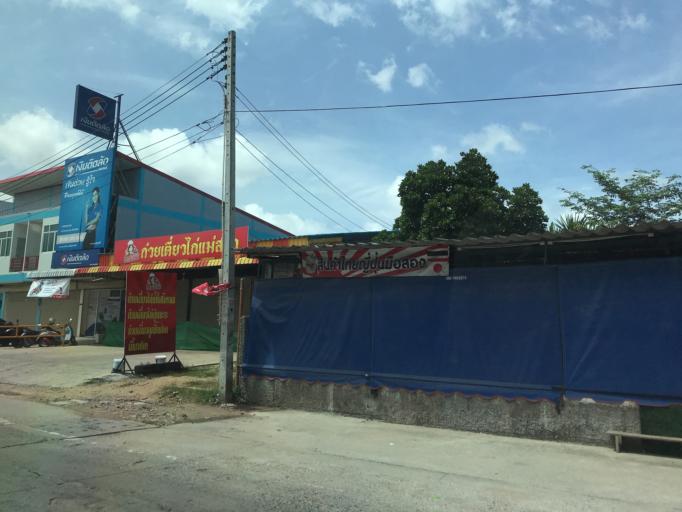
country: TH
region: Chon Buri
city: Si Racha
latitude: 13.1472
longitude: 100.9511
